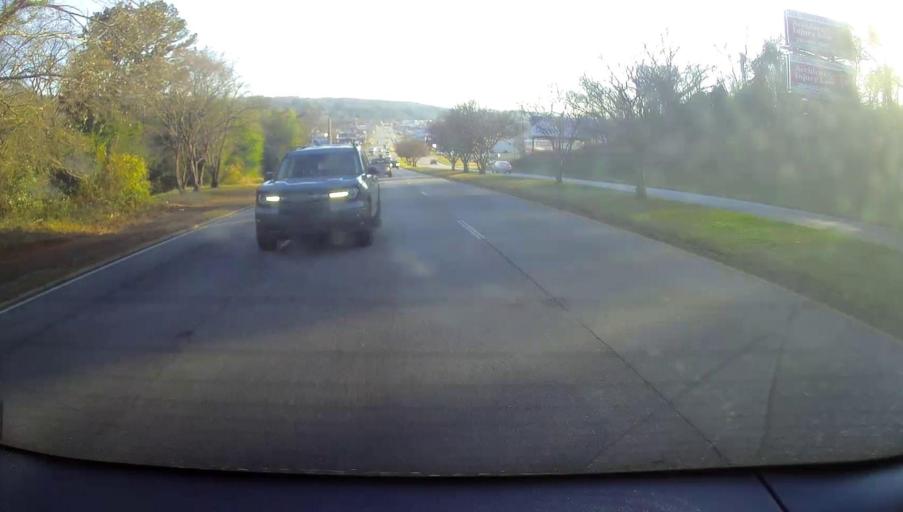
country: US
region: Alabama
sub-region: Calhoun County
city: Anniston
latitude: 33.6482
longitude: -85.8264
